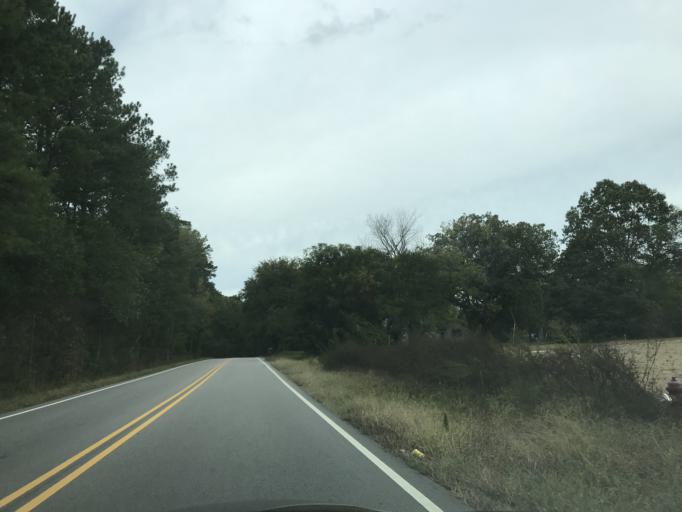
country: US
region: North Carolina
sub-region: Wake County
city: Knightdale
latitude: 35.8154
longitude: -78.4999
